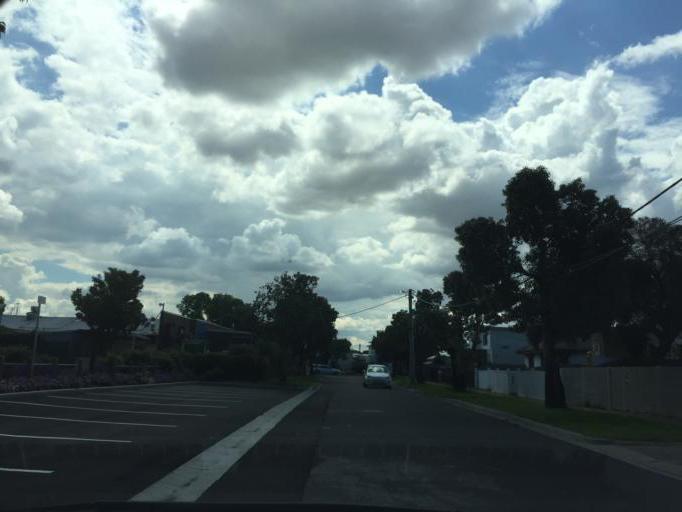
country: AU
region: Victoria
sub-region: Maribyrnong
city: Maidstone
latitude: -37.7901
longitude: 144.8691
